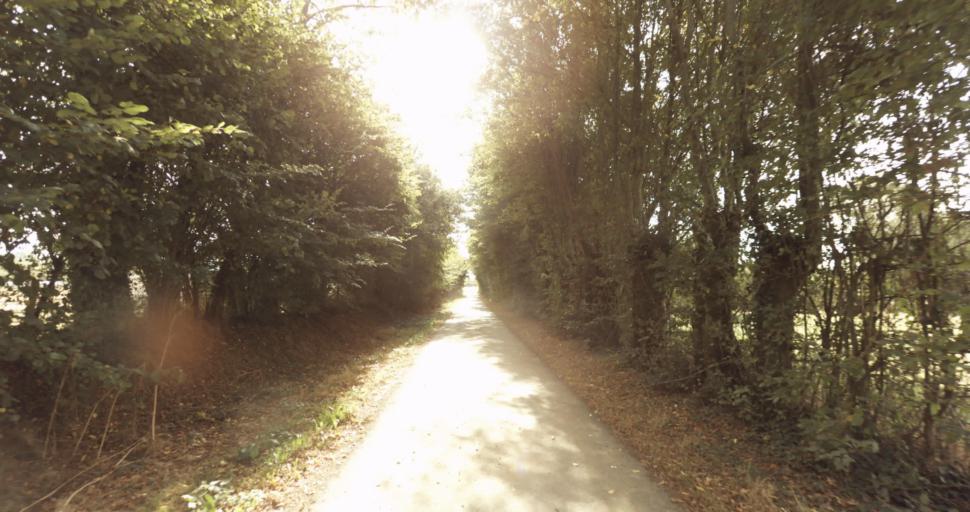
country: FR
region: Lower Normandy
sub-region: Departement de l'Orne
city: Vimoutiers
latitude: 48.9329
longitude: 0.2520
